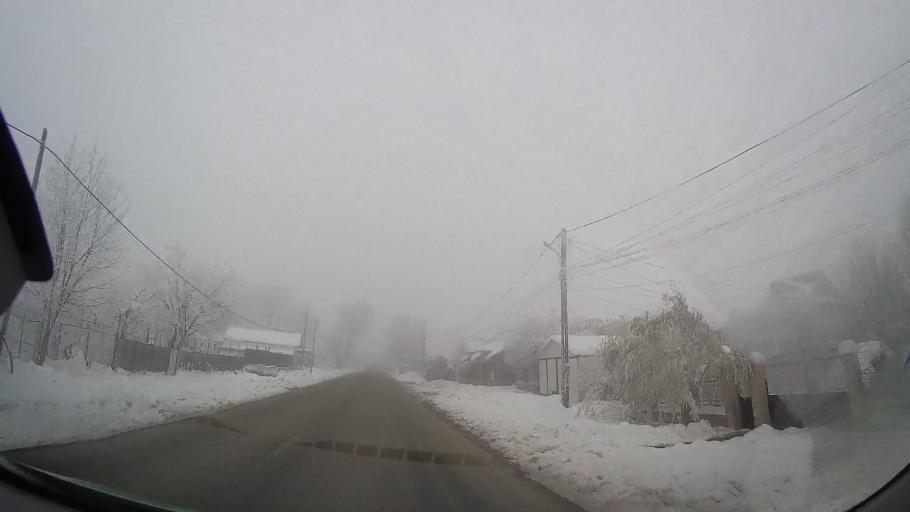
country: RO
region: Neamt
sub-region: Comuna Sabaoani
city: Sabaoani
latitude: 47.0219
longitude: 26.8640
